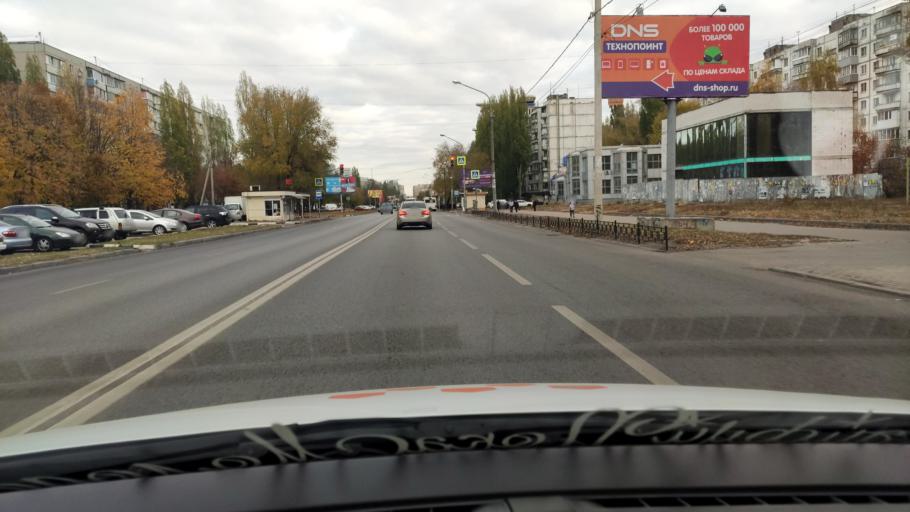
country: RU
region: Voronezj
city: Podgornoye
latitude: 51.7057
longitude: 39.1538
